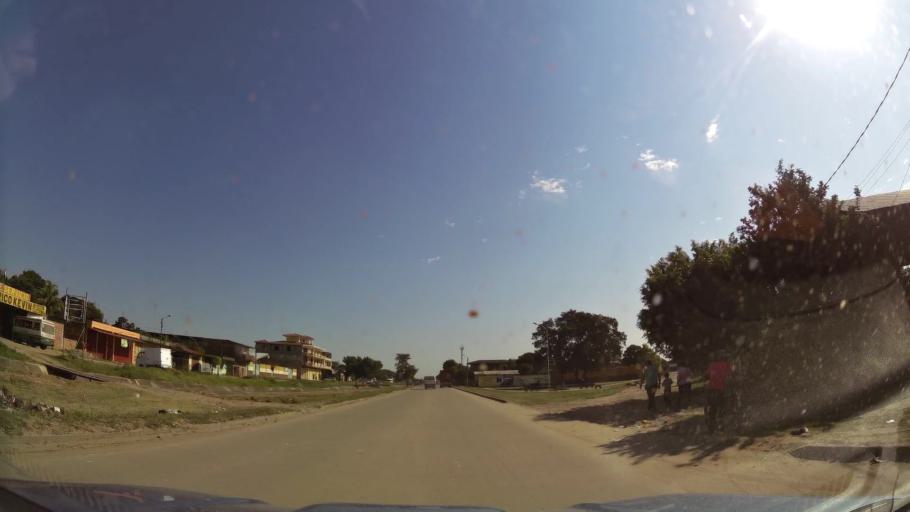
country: BO
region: Santa Cruz
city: Cotoca
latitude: -17.8145
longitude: -63.1114
